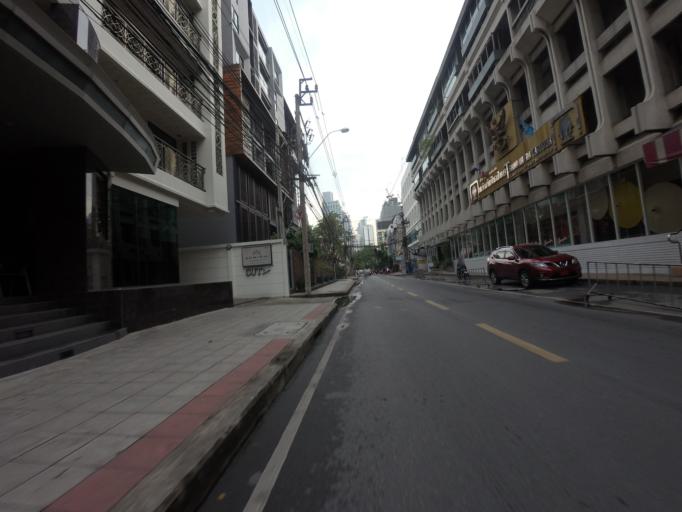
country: TH
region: Bangkok
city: Watthana
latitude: 13.7393
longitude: 100.5642
